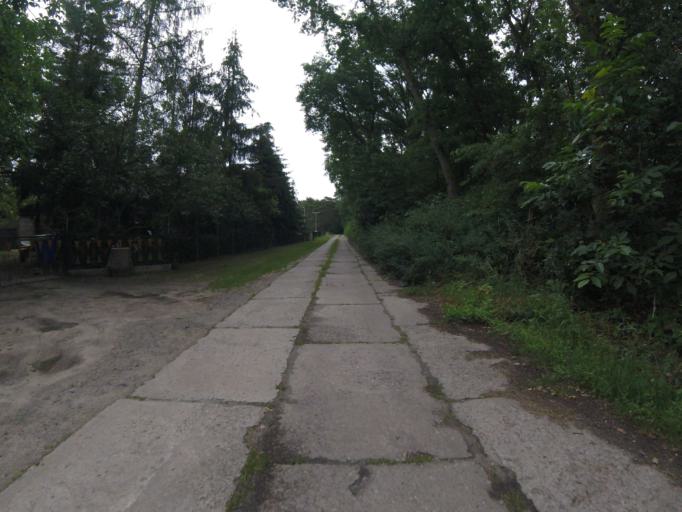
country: DE
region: Brandenburg
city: Konigs Wusterhausen
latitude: 52.3008
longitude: 13.6385
